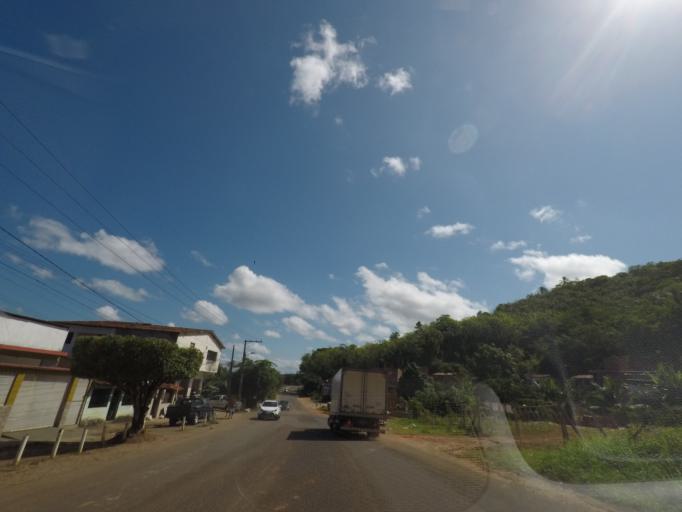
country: BR
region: Bahia
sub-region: Itubera
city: Itubera
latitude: -13.7477
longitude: -39.1528
